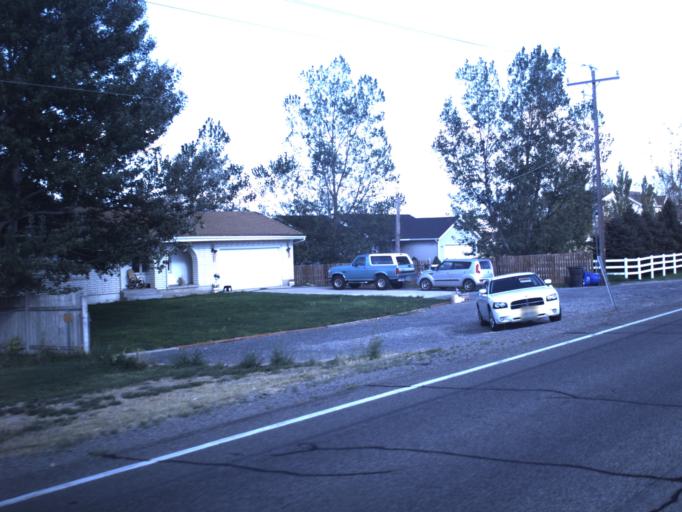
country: US
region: Utah
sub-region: Tooele County
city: Grantsville
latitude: 40.6112
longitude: -112.4937
